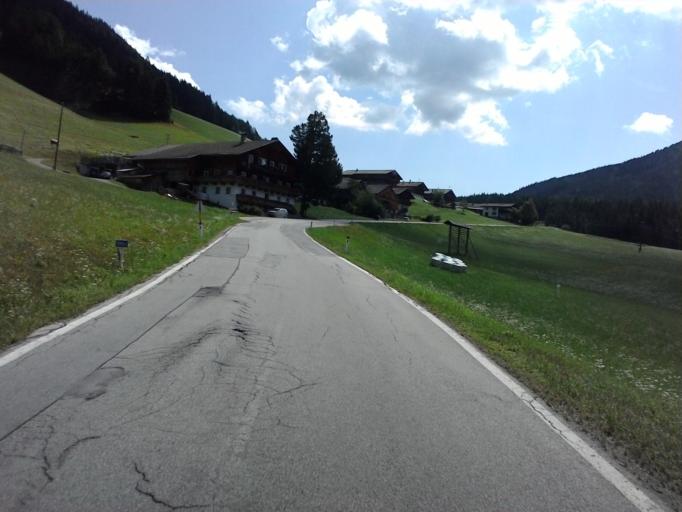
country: AT
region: Tyrol
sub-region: Politischer Bezirk Lienz
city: Kartitsch
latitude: 46.7214
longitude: 12.5176
